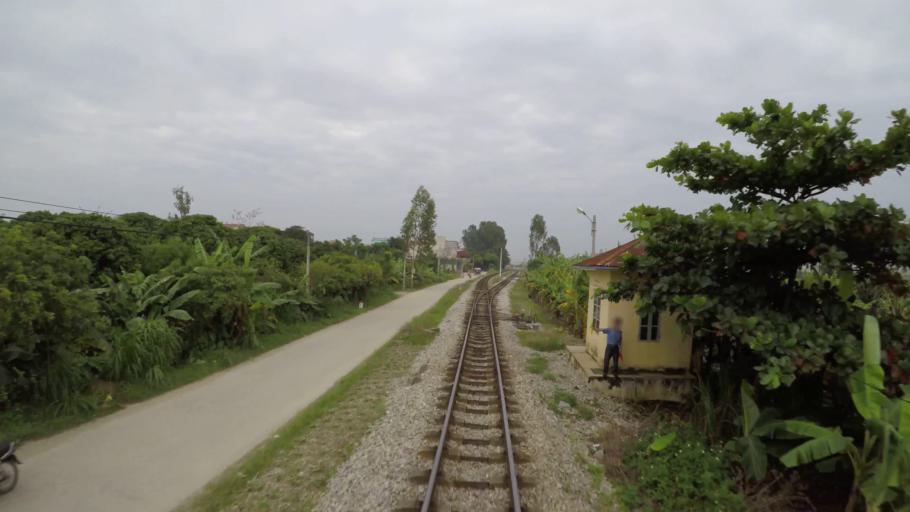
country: VN
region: Hai Duong
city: Lai Cach
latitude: 20.9491
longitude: 106.2496
